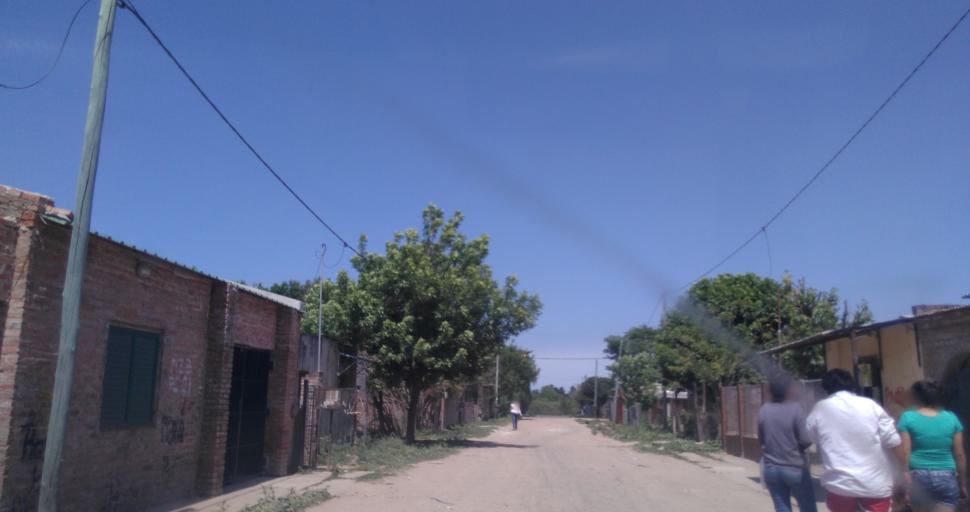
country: AR
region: Chaco
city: Resistencia
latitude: -27.4189
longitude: -58.9805
